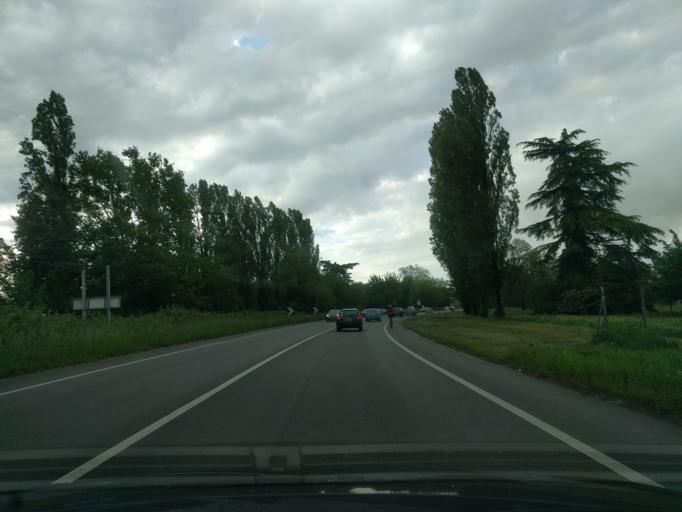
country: IT
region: Emilia-Romagna
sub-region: Provincia di Ferrara
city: Ferrara
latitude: 44.8663
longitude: 11.6014
